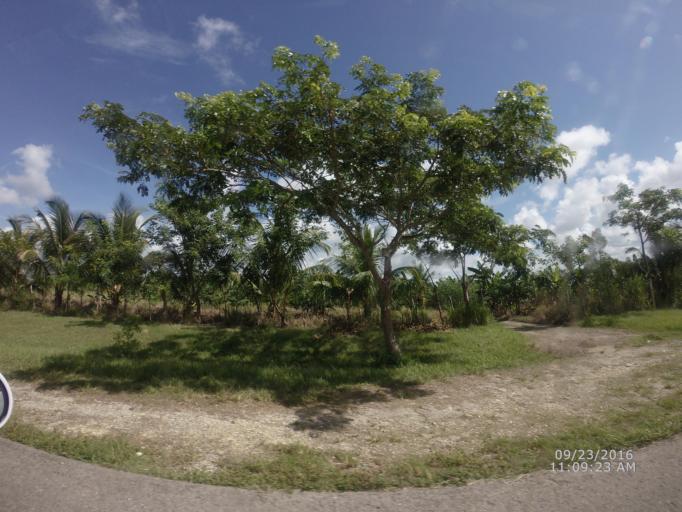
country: CU
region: La Habana
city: Arroyo Naranjo
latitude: 23.0180
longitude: -82.2439
